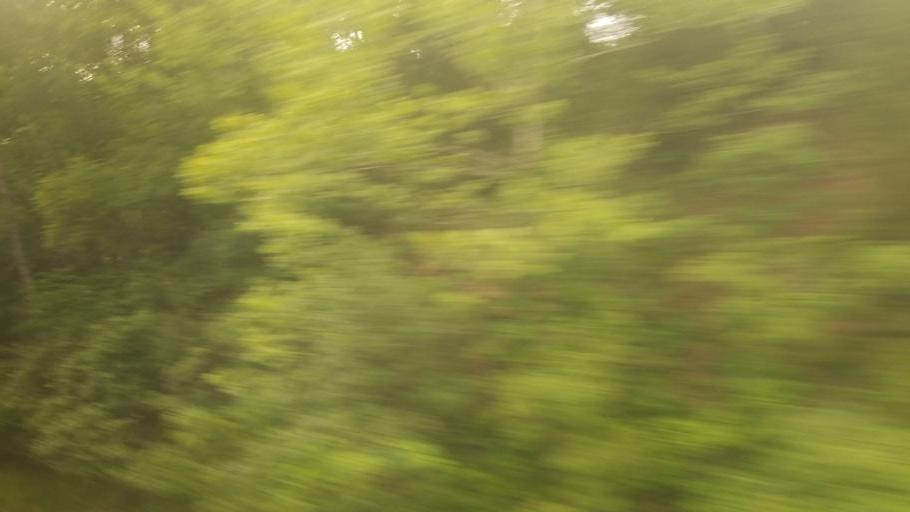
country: US
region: Kansas
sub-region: Shawnee County
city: Topeka
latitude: 39.0550
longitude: -95.4825
